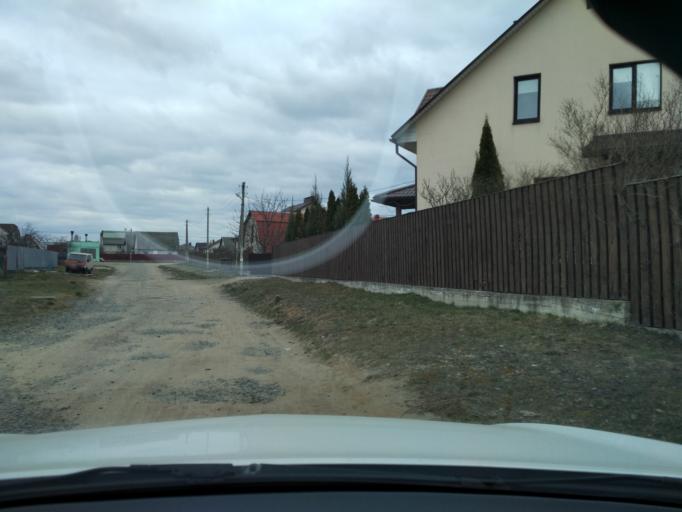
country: BY
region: Minsk
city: Bal'shavik
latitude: 53.9671
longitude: 27.5885
